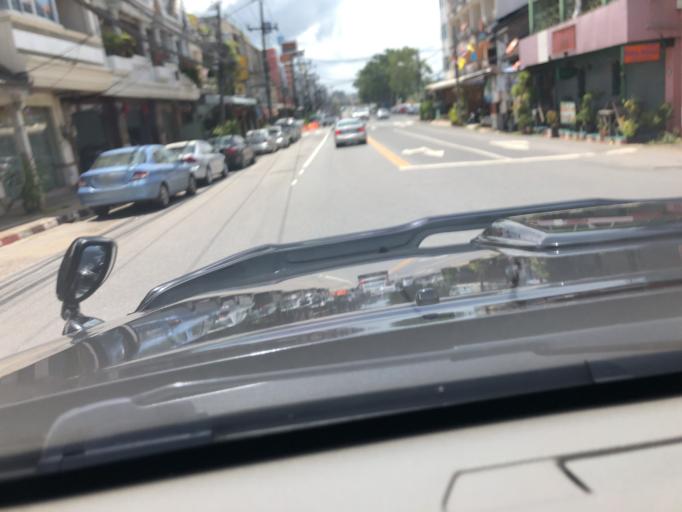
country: TH
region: Krabi
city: Krabi
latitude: 8.0630
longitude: 98.9180
